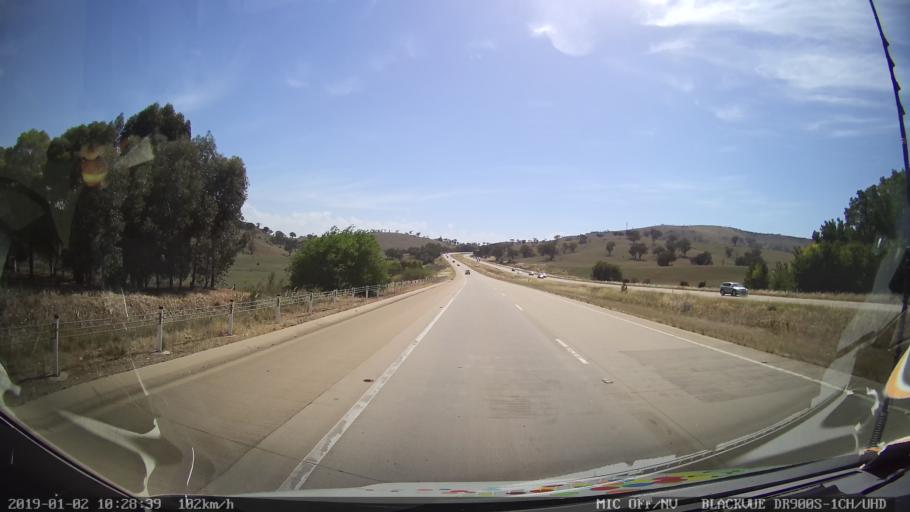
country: AU
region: New South Wales
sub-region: Gundagai
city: Gundagai
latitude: -34.9019
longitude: 148.1943
